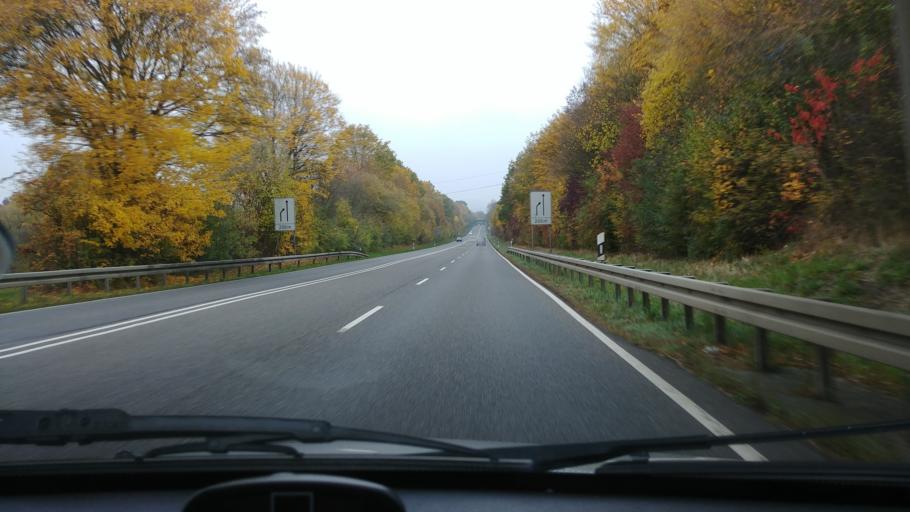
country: DE
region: Hesse
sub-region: Regierungsbezirk Giessen
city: Dehrn
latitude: 50.4577
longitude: 8.0774
